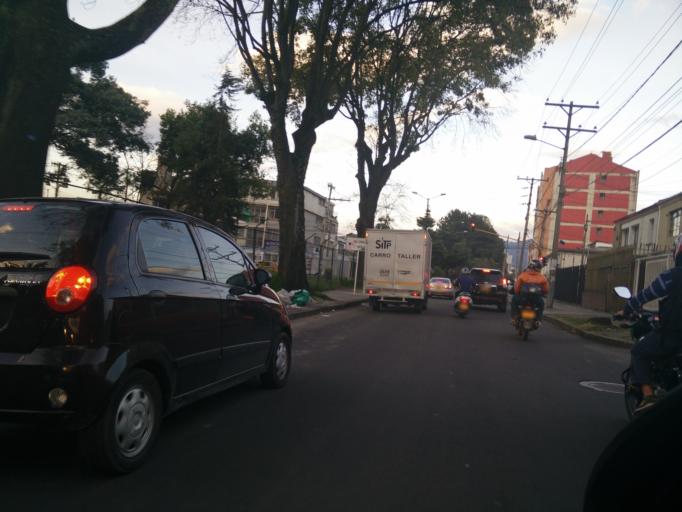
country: CO
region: Bogota D.C.
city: Bogota
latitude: 4.6473
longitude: -74.0735
